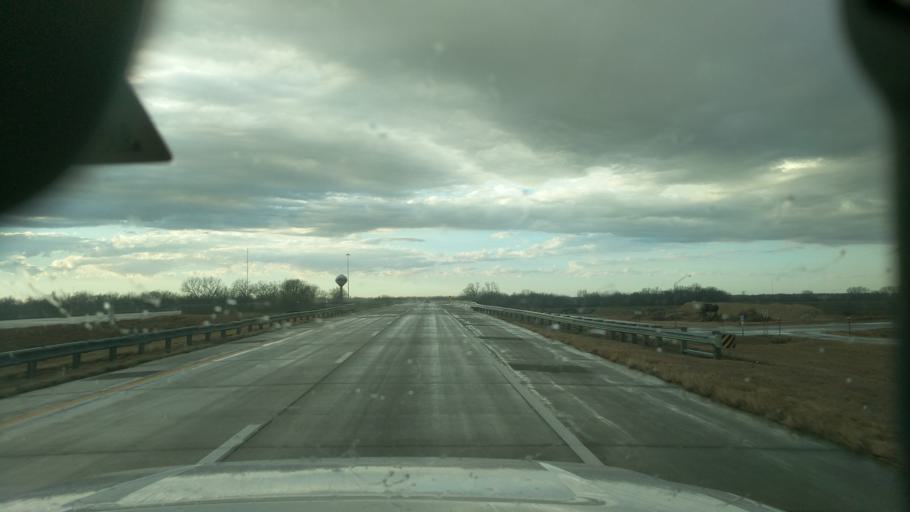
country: US
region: Kansas
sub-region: Harvey County
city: North Newton
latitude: 38.0840
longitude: -97.3448
